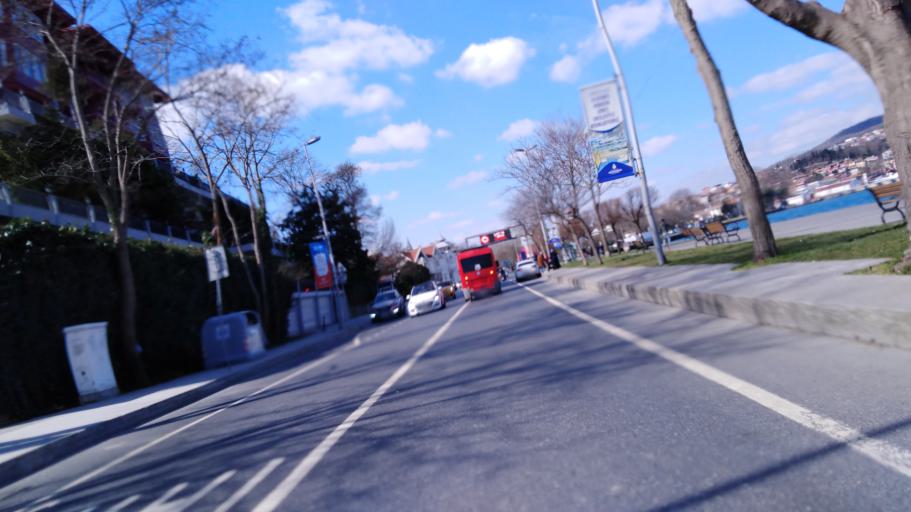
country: TR
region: Istanbul
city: Arikoey
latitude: 41.1531
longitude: 29.0399
